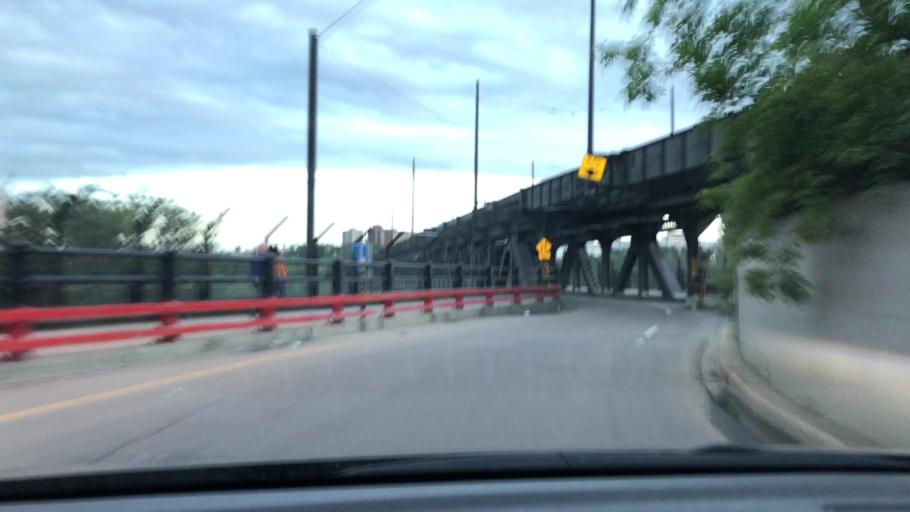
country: CA
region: Alberta
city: Edmonton
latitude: 53.5327
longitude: -113.5094
